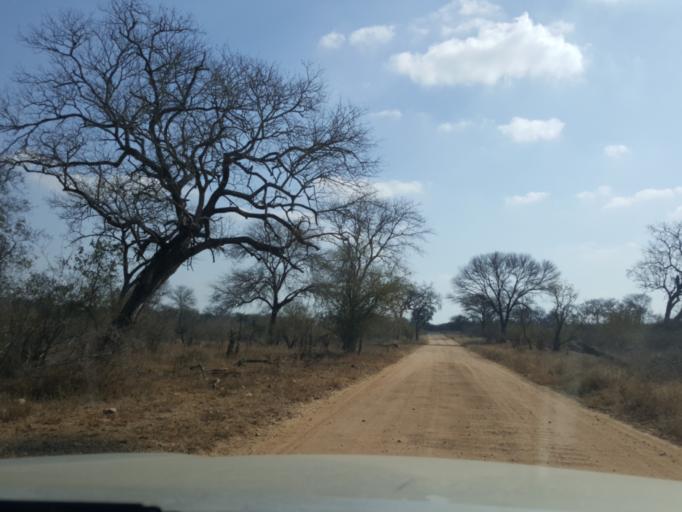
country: ZA
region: Mpumalanga
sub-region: Ehlanzeni District
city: Komatipoort
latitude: -25.2708
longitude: 31.8041
